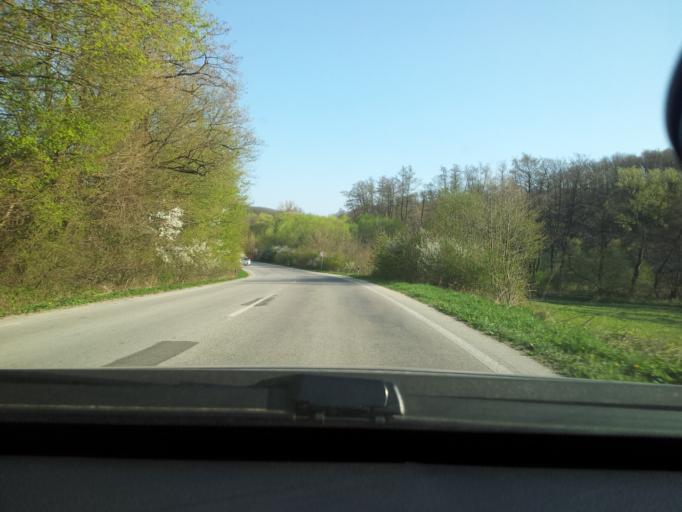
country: SK
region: Nitriansky
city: Zlate Moravce
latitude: 48.4498
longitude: 18.4129
